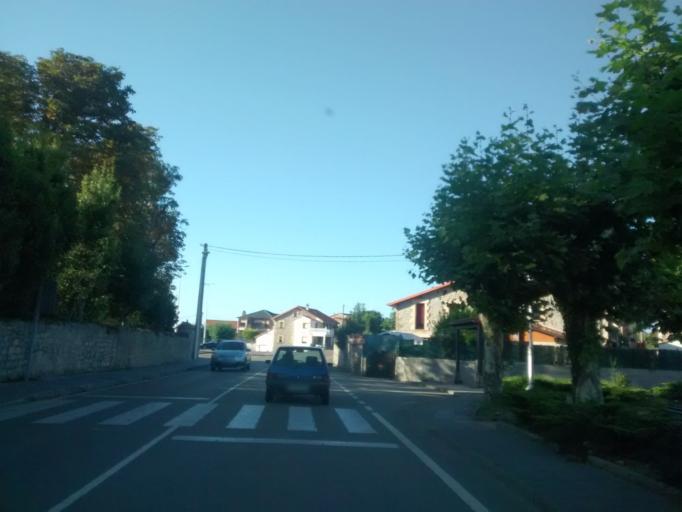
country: ES
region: Cantabria
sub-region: Provincia de Cantabria
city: Santander
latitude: 43.4350
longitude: -3.7708
